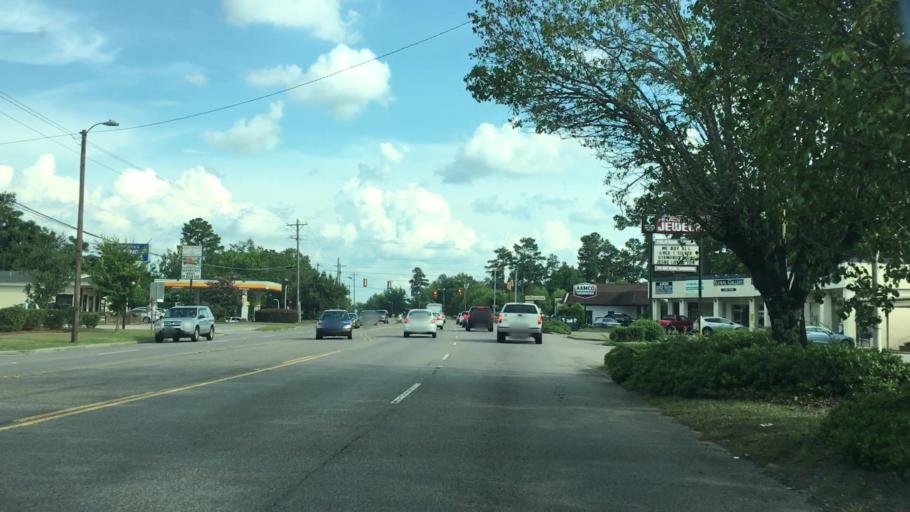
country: US
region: South Carolina
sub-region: Aiken County
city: Aiken
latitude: 33.5318
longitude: -81.7242
